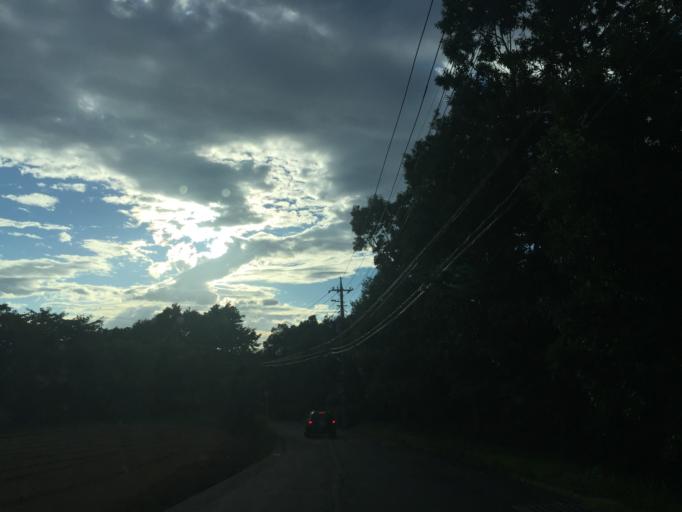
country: JP
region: Shizuoka
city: Mishima
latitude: 35.1580
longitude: 138.9260
